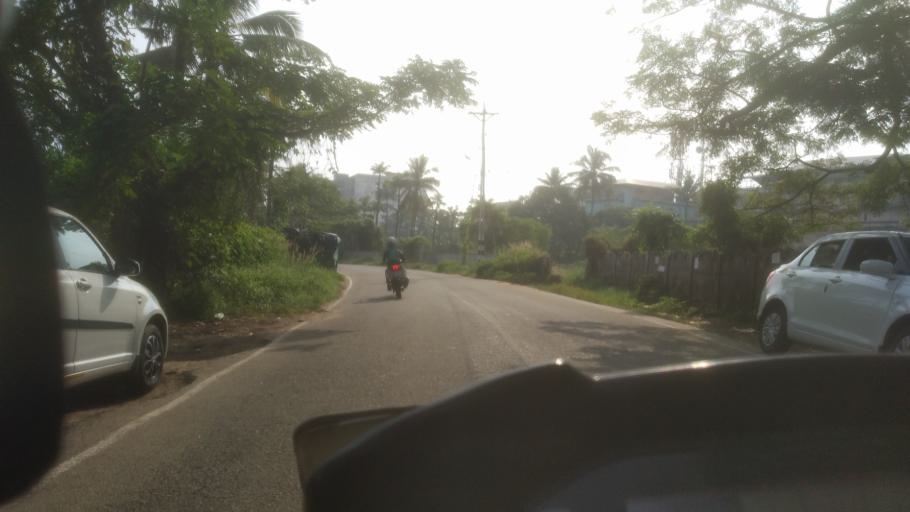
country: IN
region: Kerala
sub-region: Ernakulam
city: Angamali
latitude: 10.1607
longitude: 76.3871
